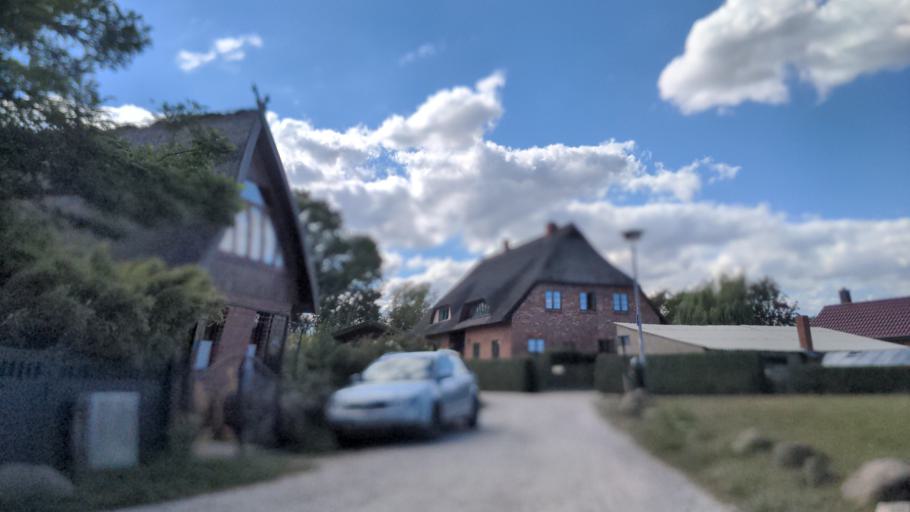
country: DE
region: Mecklenburg-Vorpommern
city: Wismar
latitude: 53.9187
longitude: 11.4076
